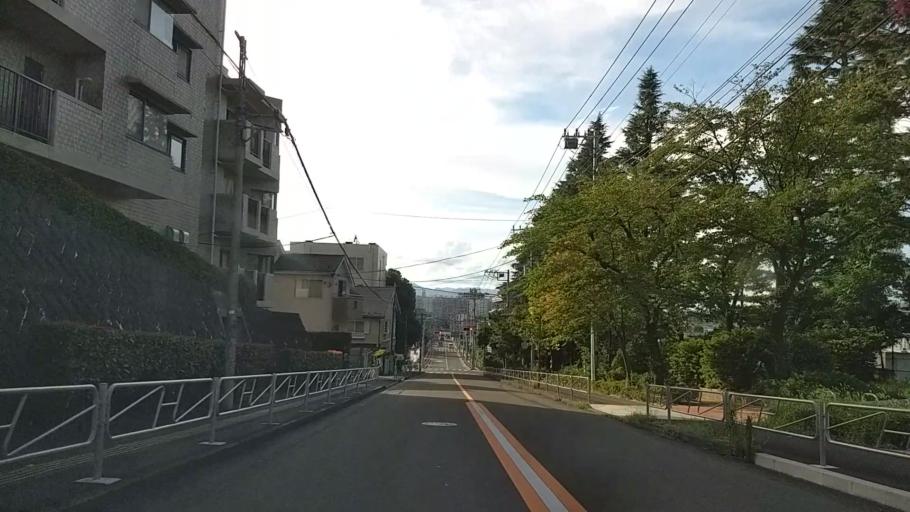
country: JP
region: Tokyo
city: Hachioji
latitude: 35.6503
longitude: 139.3211
